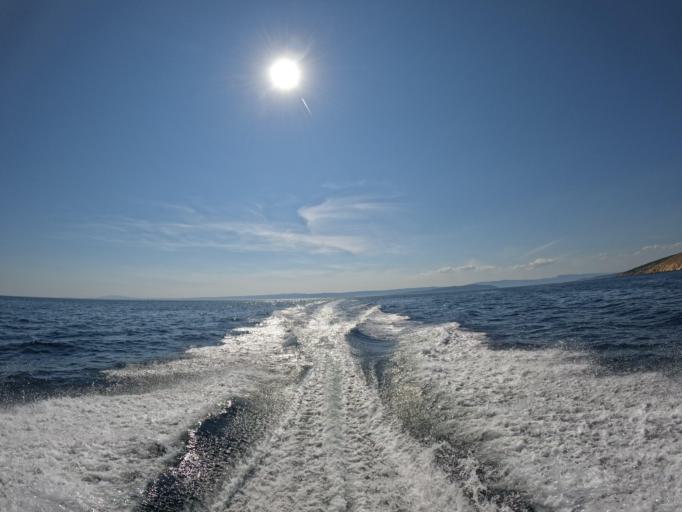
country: HR
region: Primorsko-Goranska
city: Punat
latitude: 44.9614
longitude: 14.6517
